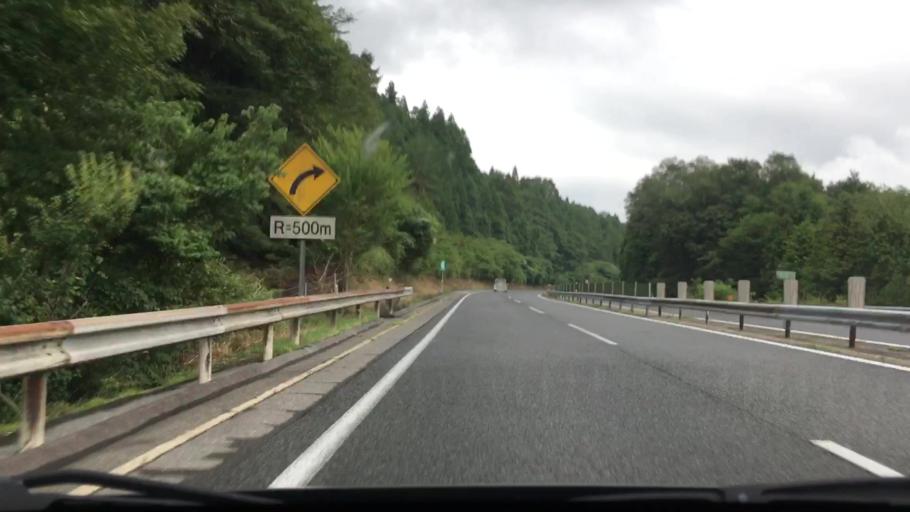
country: JP
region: Hiroshima
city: Miyoshi
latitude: 34.7014
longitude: 132.6085
